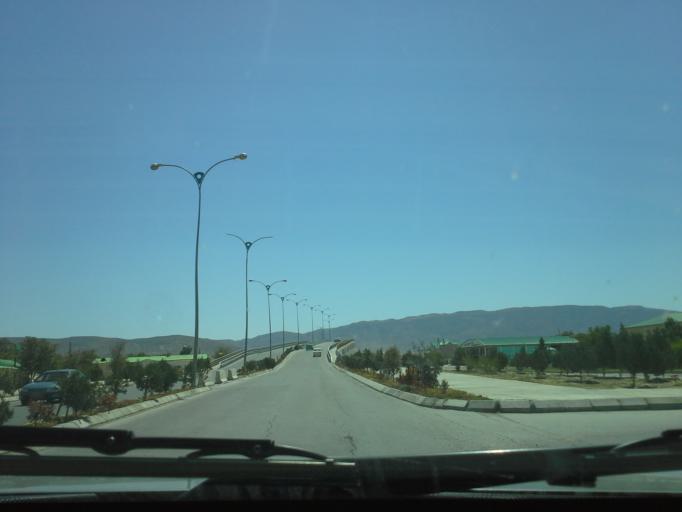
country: TM
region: Balkan
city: Serdar
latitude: 38.9819
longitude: 56.2793
